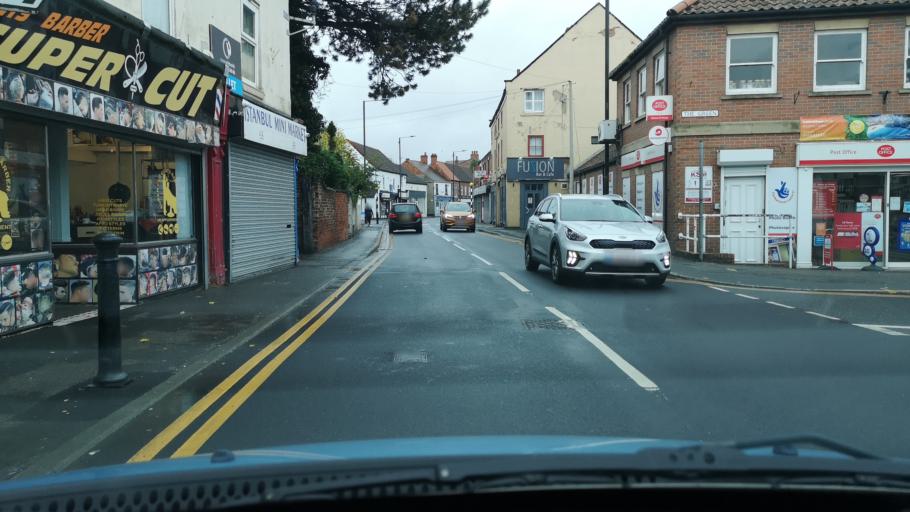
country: GB
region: England
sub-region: Doncaster
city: Hatfield
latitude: 53.6120
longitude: -0.9627
